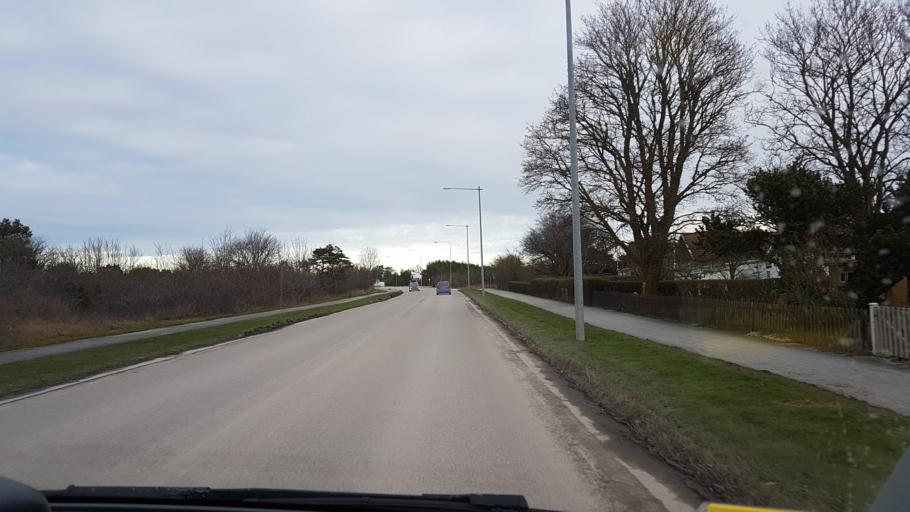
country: SE
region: Gotland
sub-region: Gotland
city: Visby
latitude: 57.6498
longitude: 18.3150
